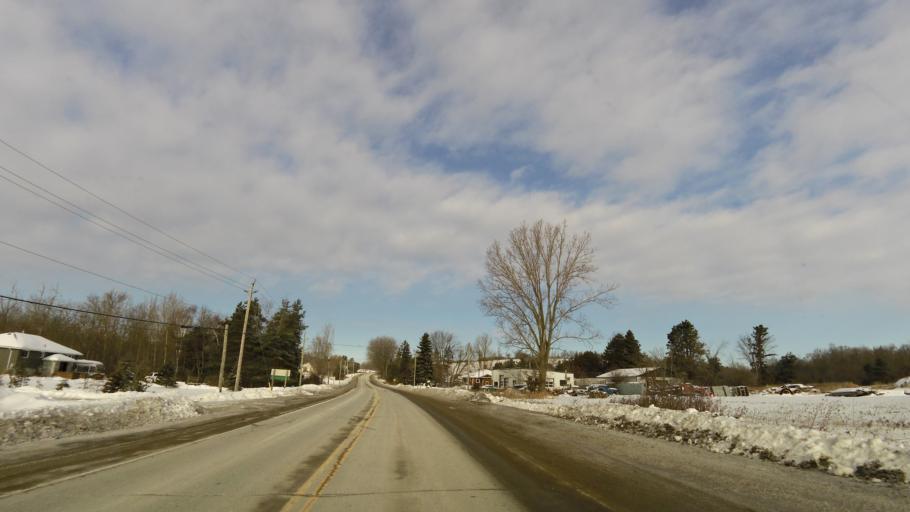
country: CA
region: Ontario
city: Quinte West
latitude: 44.0786
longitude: -77.7714
